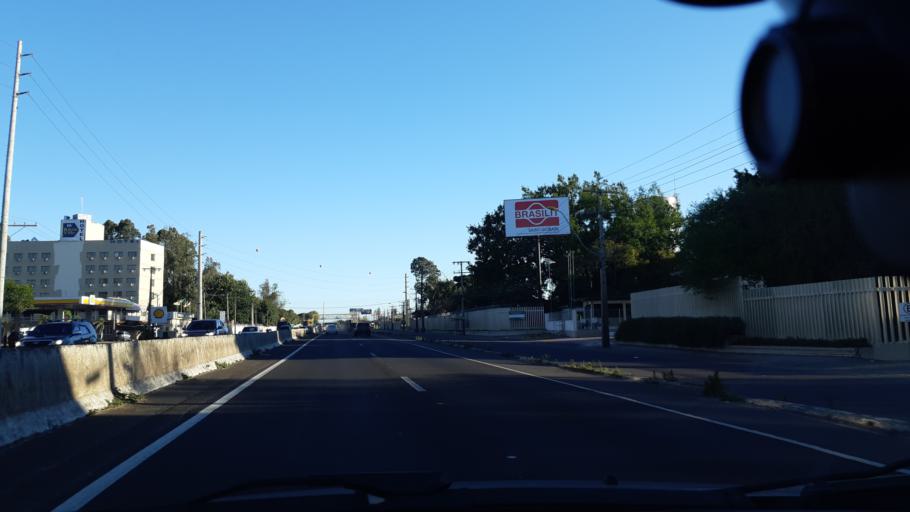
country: BR
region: Rio Grande do Sul
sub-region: Esteio
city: Esteio
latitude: -29.8394
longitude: -51.1761
